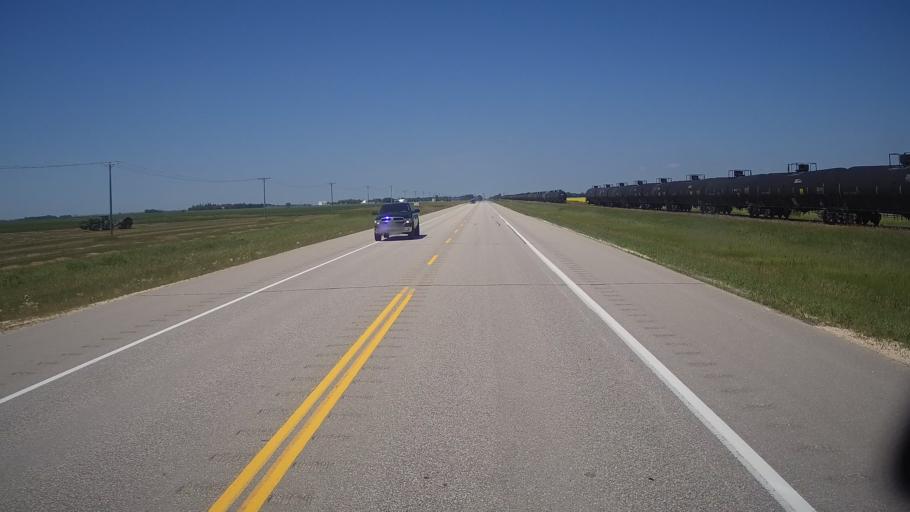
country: CA
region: Manitoba
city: Stonewall
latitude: 50.1105
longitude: -97.5150
